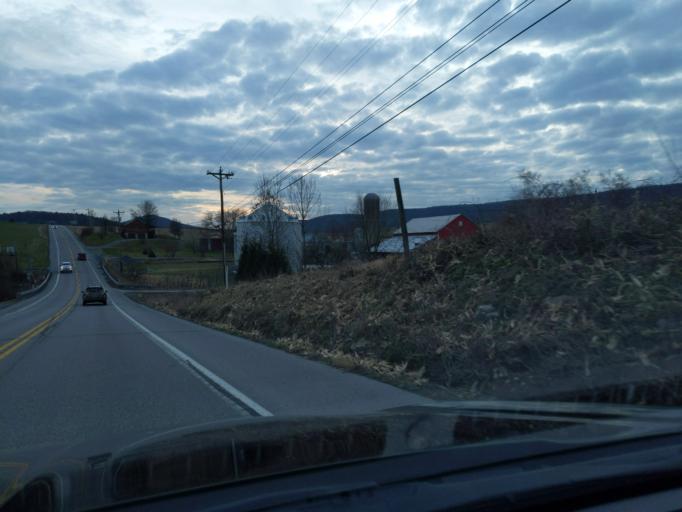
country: US
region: Pennsylvania
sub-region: Blair County
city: Williamsburg
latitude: 40.5267
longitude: -78.1990
